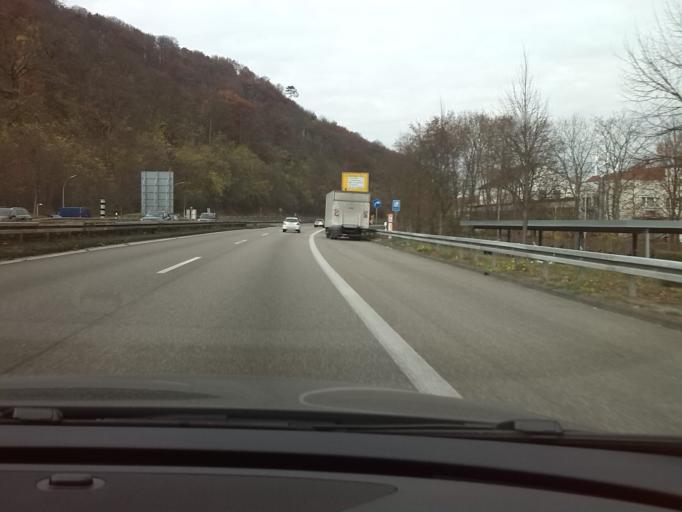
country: DE
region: Baden-Wuerttemberg
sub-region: Regierungsbezirk Stuttgart
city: Ostfildern
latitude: 48.7430
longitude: 9.2687
